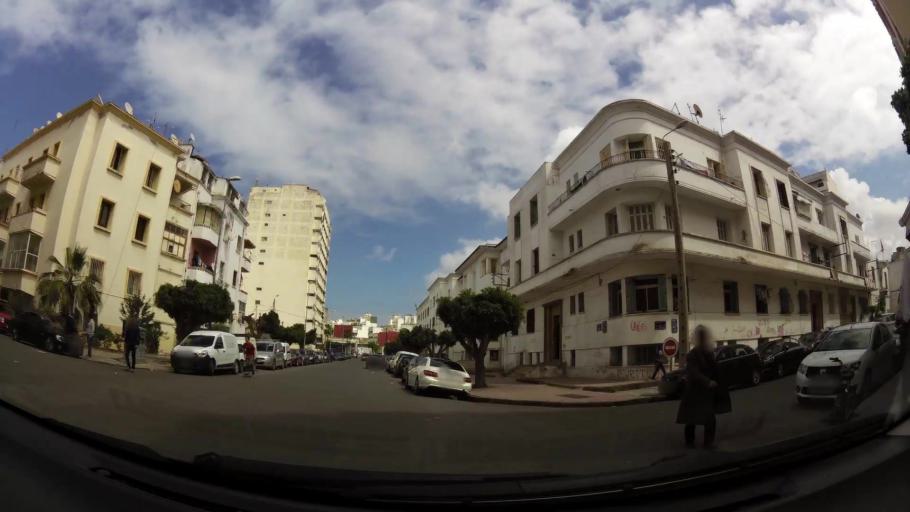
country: MA
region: Grand Casablanca
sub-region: Casablanca
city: Casablanca
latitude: 33.5963
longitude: -7.6398
